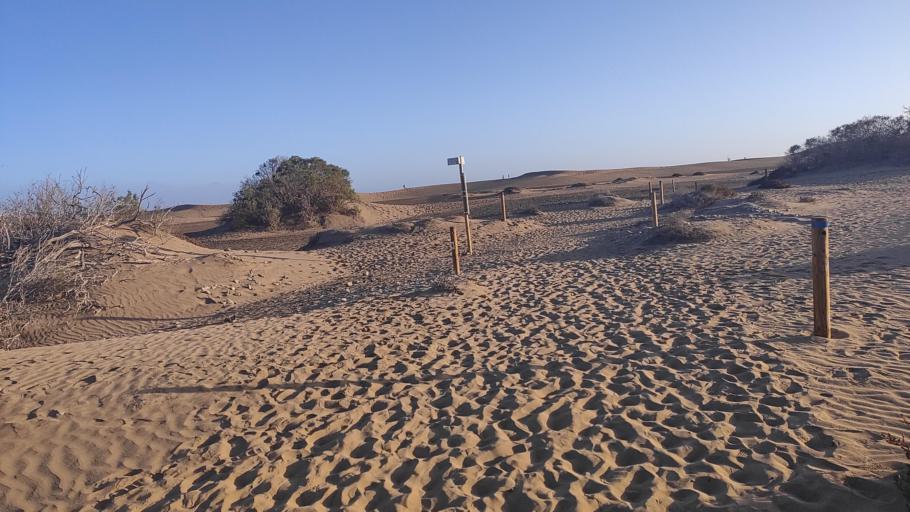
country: ES
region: Canary Islands
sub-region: Provincia de Las Palmas
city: Playa del Ingles
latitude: 27.7393
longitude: -15.5853
